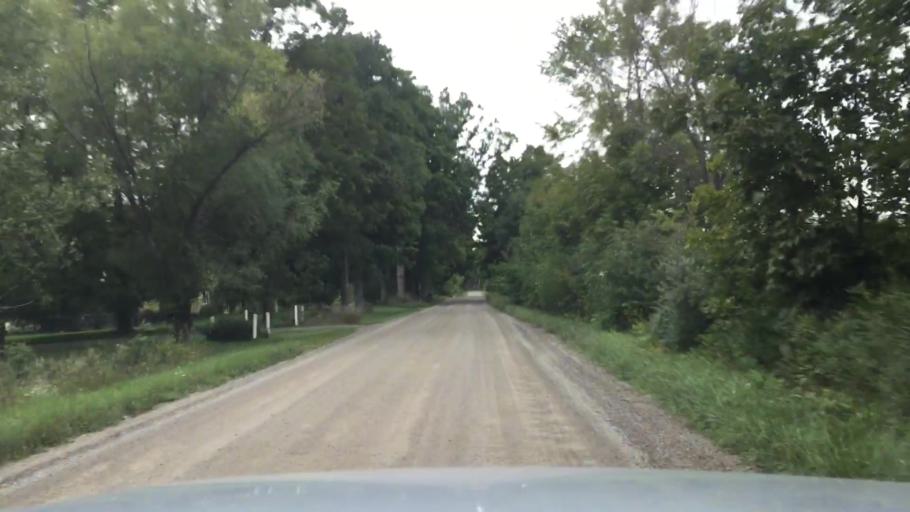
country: US
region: Michigan
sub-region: Shiawassee County
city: Corunna
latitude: 42.9315
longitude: -84.1047
